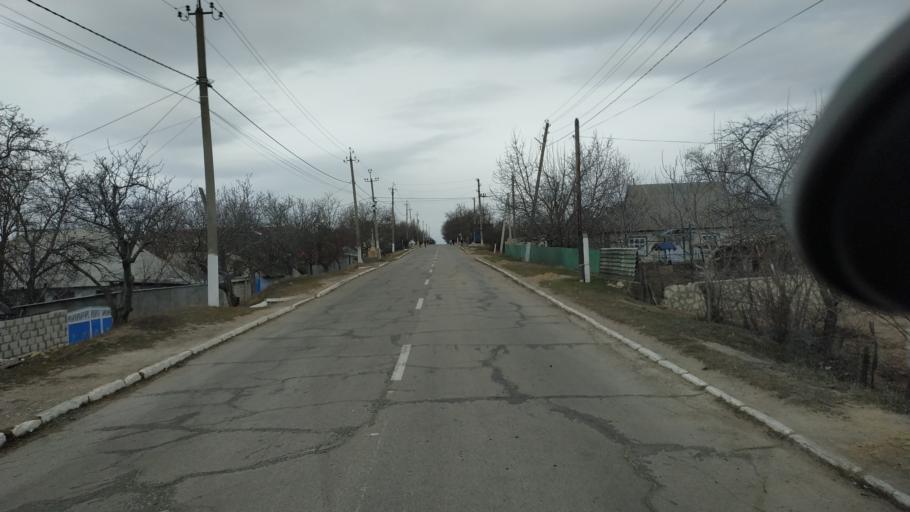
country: MD
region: Telenesti
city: Cocieri
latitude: 47.3510
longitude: 29.1171
